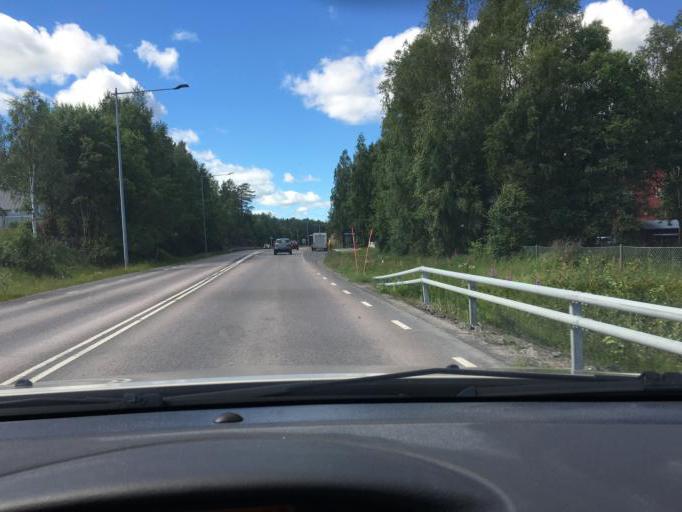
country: SE
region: Norrbotten
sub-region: Lulea Kommun
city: Bergnaset
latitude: 65.5777
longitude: 22.1119
